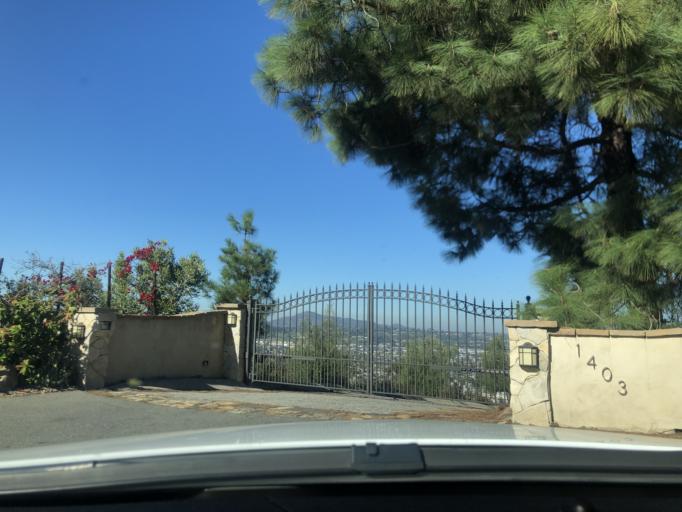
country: US
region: California
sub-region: San Diego County
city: Casa de Oro-Mount Helix
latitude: 32.7747
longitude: -116.9499
